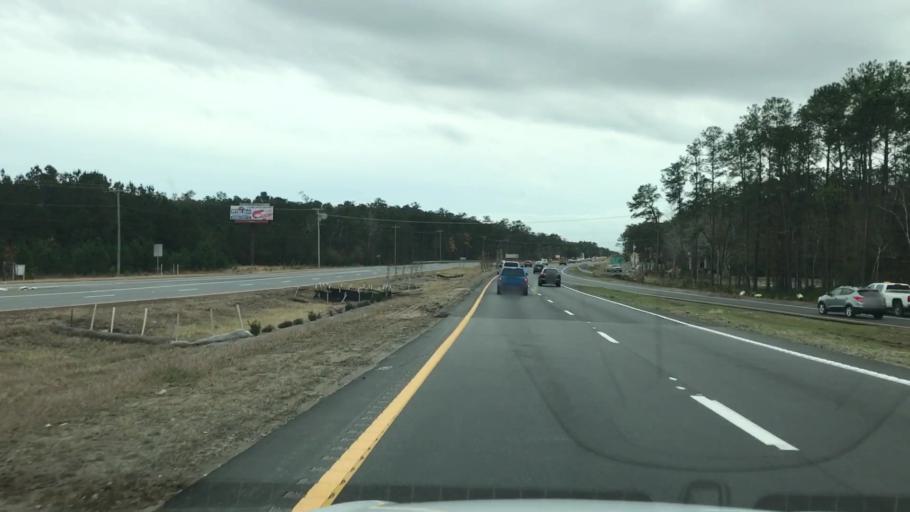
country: US
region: South Carolina
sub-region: Horry County
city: Garden City
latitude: 33.6193
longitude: -79.0059
